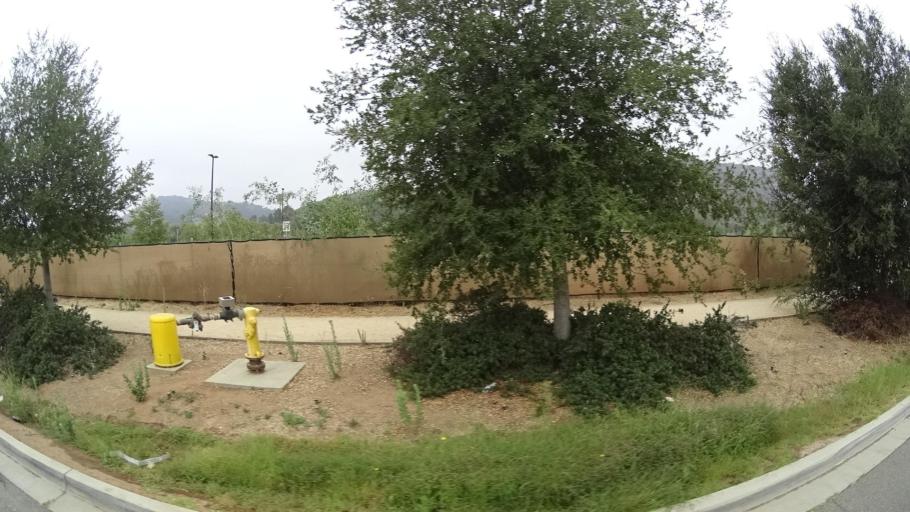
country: US
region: California
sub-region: San Diego County
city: Rainbow
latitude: 33.3511
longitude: -117.1551
